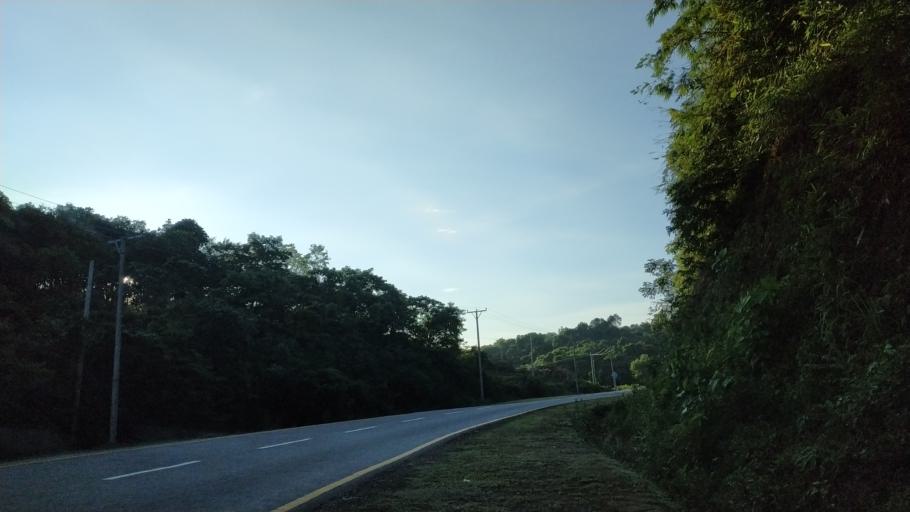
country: MM
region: Tanintharyi
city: Dawei
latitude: 14.2893
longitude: 98.2110
